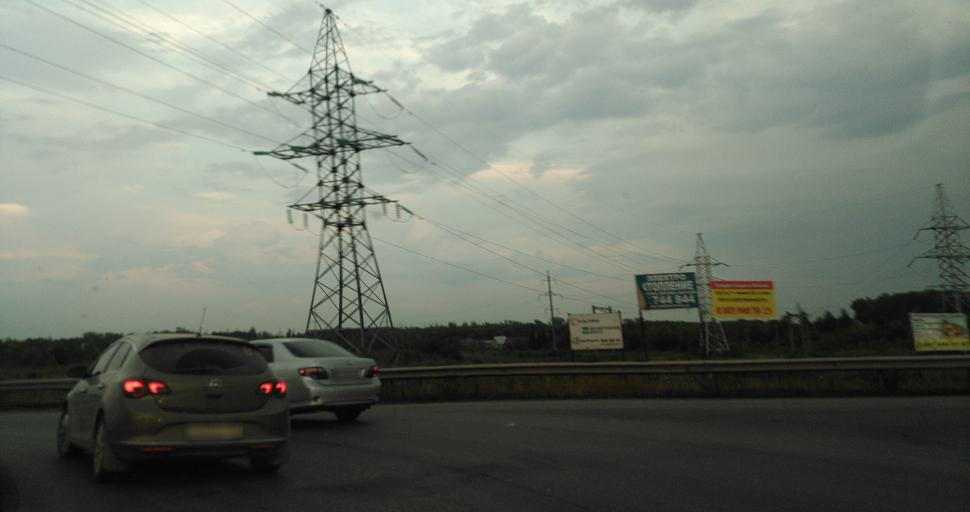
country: RU
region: Bashkortostan
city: Ufa
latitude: 54.6683
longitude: 55.9247
